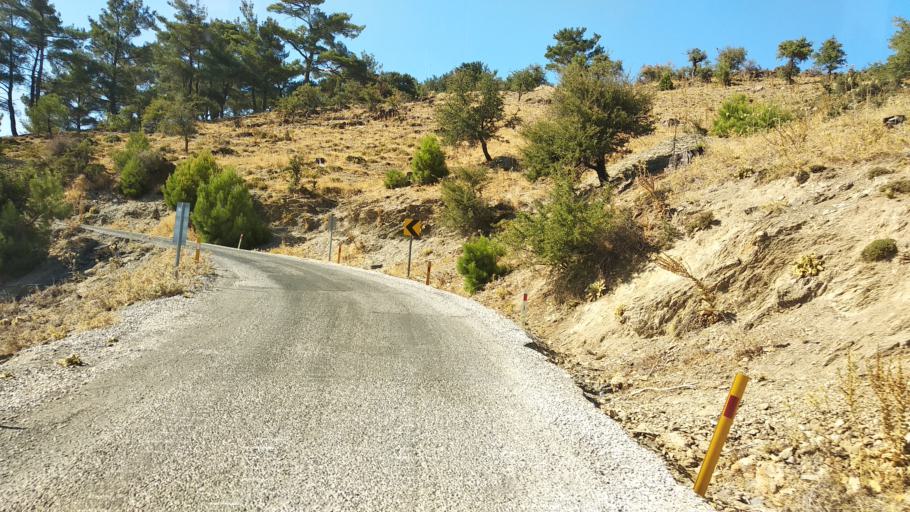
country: TR
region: Izmir
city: Gaziemir
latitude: 38.2957
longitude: 27.0006
